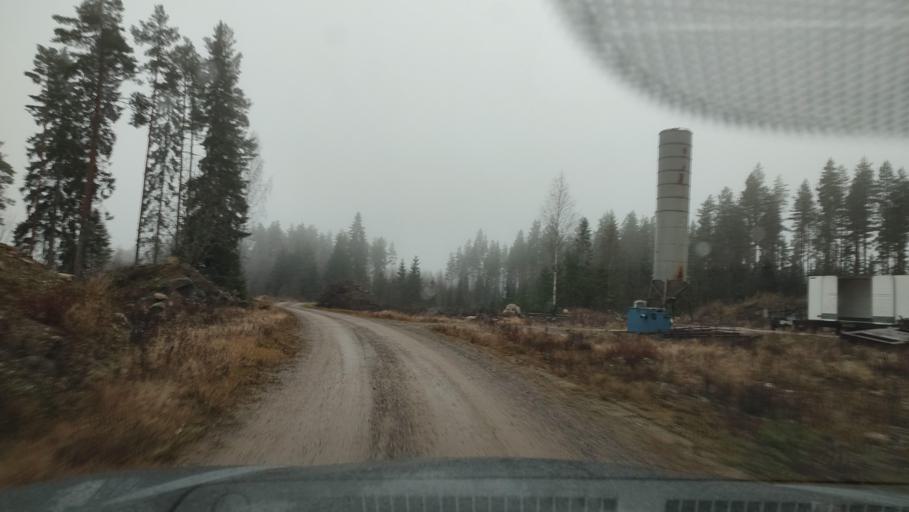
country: FI
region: Southern Ostrobothnia
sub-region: Suupohja
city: Karijoki
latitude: 62.1939
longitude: 21.7806
